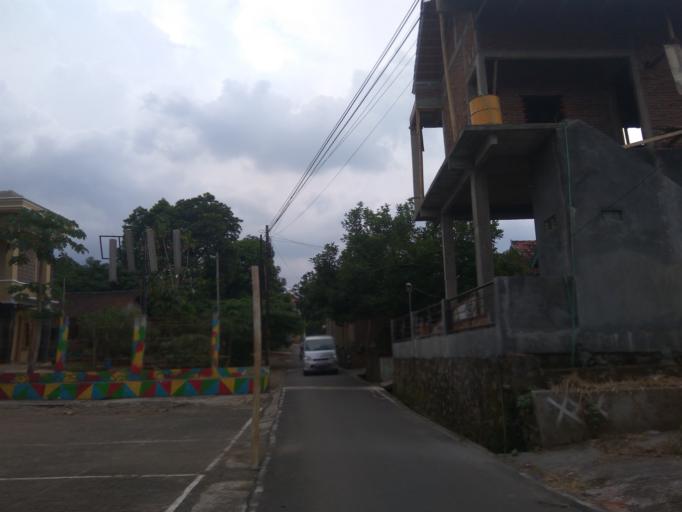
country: ID
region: Central Java
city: Semarang
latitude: -7.0636
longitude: 110.4429
